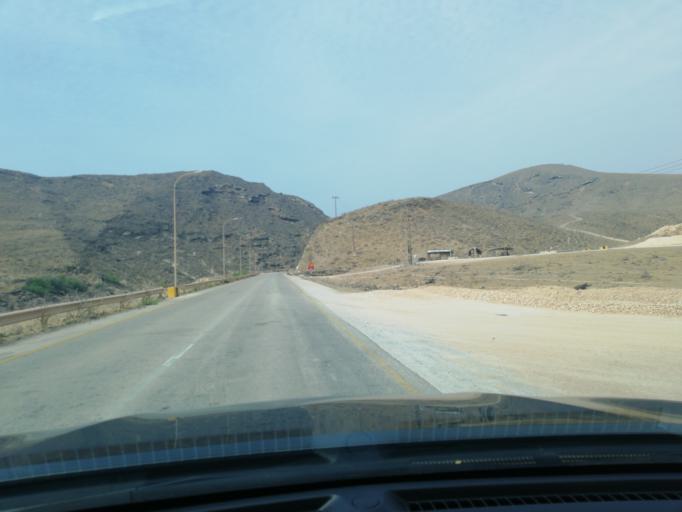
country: OM
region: Zufar
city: Salalah
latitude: 16.9016
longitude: 53.8199
